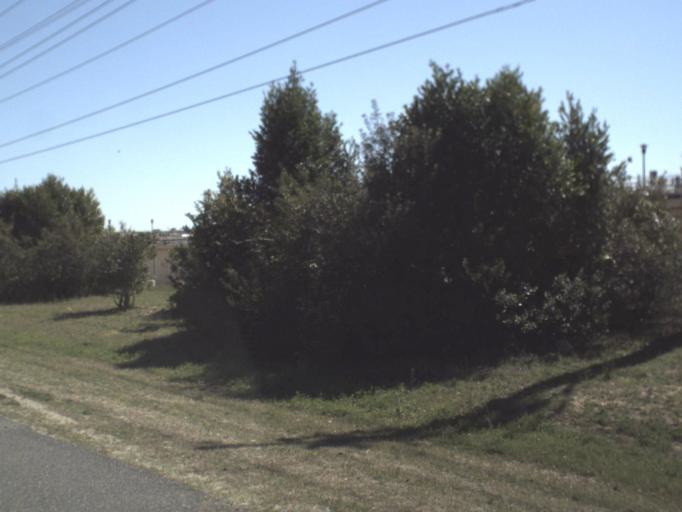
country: US
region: Florida
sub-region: Leon County
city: Tallahassee
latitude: 30.3930
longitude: -84.3208
